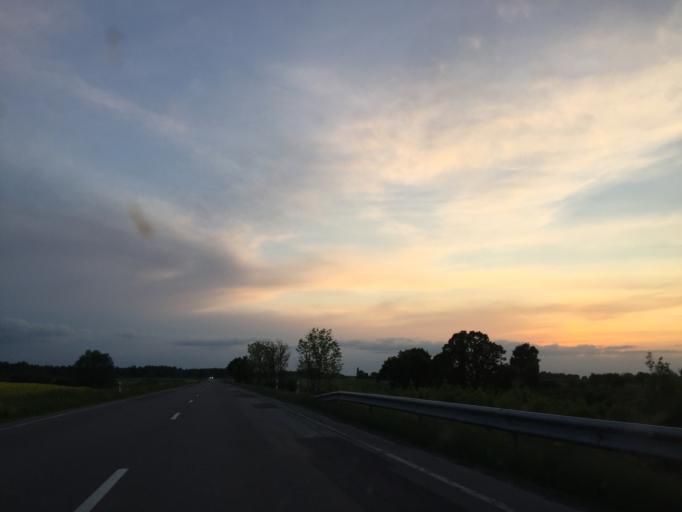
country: LT
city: Venta
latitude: 56.0054
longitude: 22.7188
